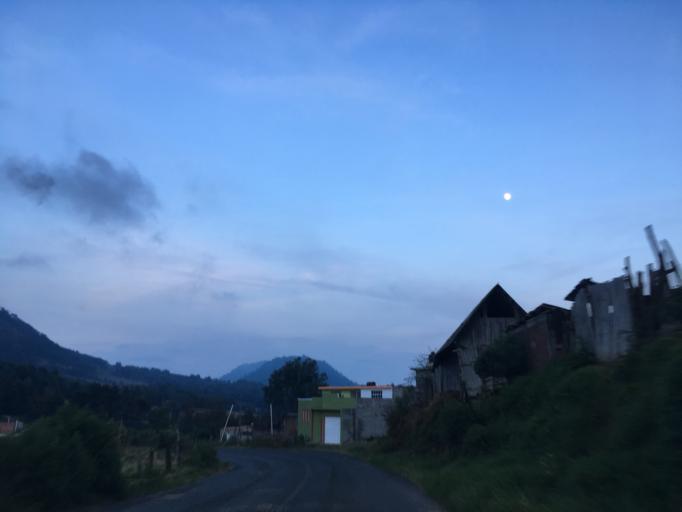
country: MX
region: Michoacan
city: Charapan
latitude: 19.6518
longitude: -102.2468
